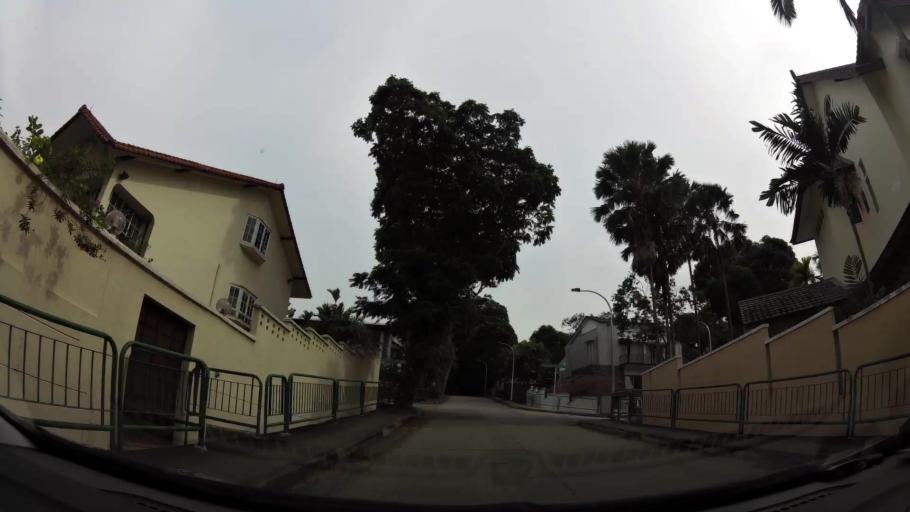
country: SG
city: Singapore
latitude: 1.3214
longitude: 103.7969
